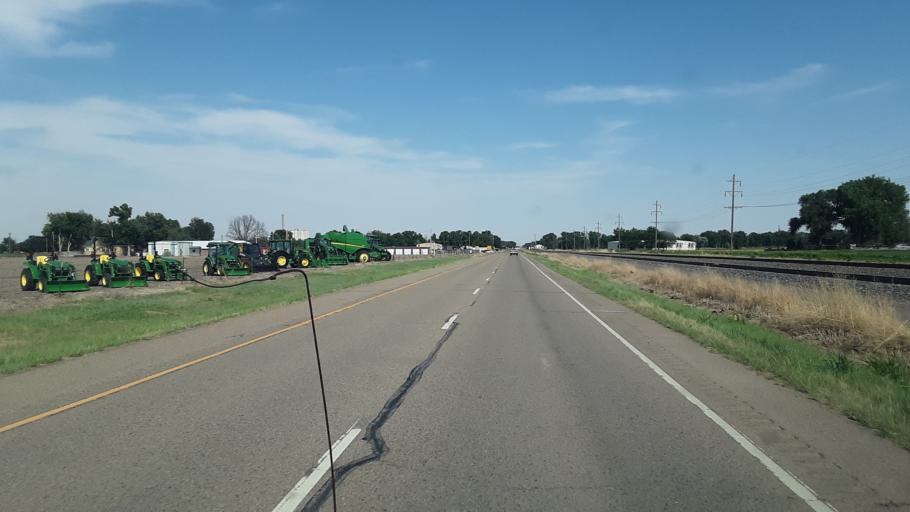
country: US
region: Colorado
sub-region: Otero County
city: Rocky Ford
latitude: 38.0620
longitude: -103.7424
